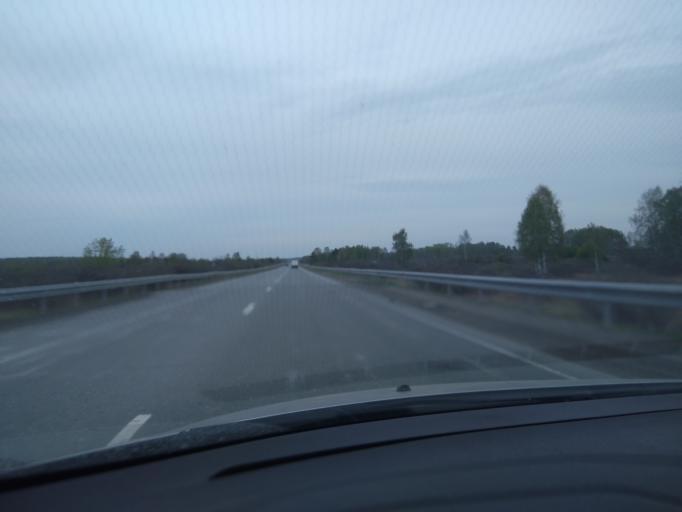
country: RU
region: Sverdlovsk
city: Yelanskiy
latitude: 56.8170
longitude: 62.5412
